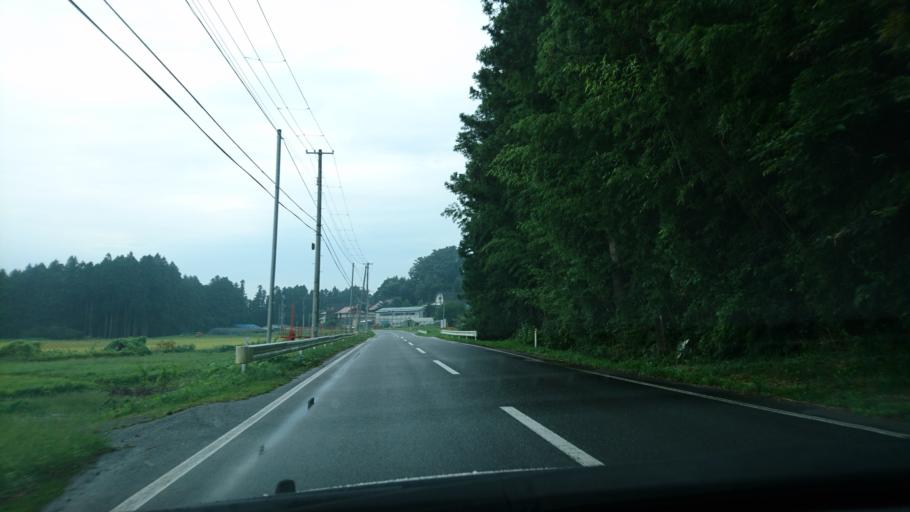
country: JP
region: Iwate
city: Ichinoseki
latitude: 38.8783
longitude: 141.2647
